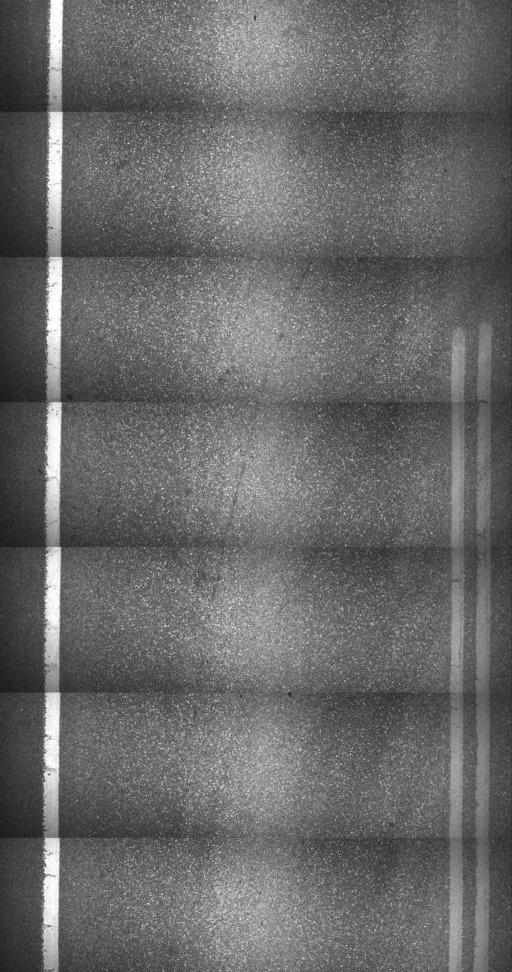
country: US
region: Vermont
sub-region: Chittenden County
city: Hinesburg
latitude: 44.2440
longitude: -73.0589
